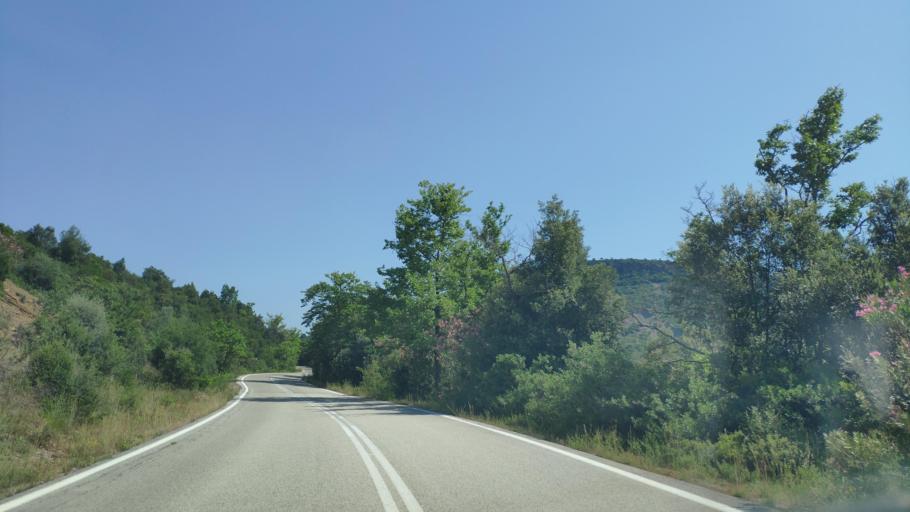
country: GR
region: West Greece
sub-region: Nomos Aitolias kai Akarnanias
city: Lepenou
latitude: 38.7780
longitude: 21.3351
